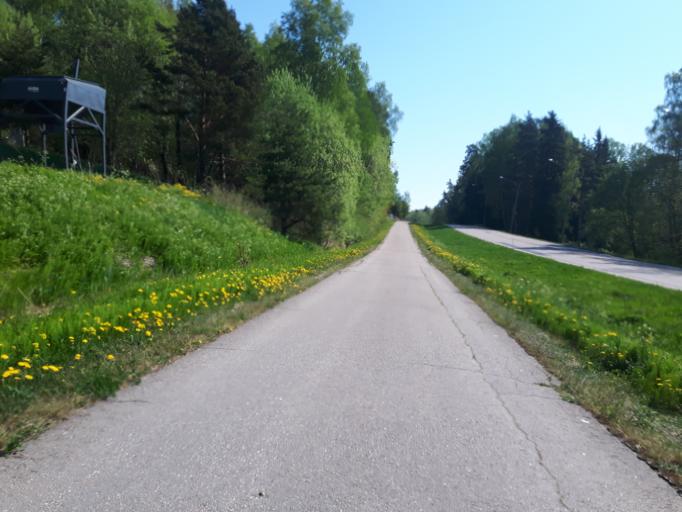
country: FI
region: Uusimaa
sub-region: Helsinki
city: Sibbo
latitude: 60.2619
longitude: 25.2420
